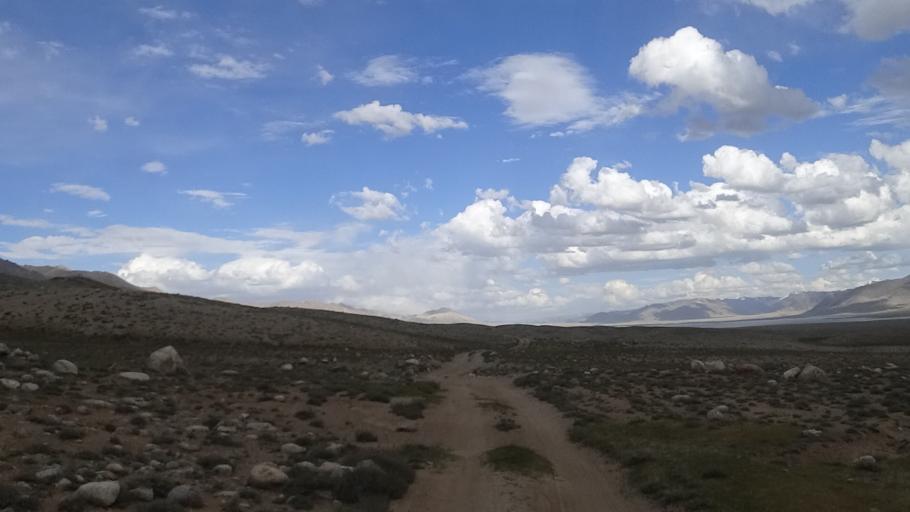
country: TJ
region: Gorno-Badakhshan
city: Murghob
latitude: 37.4690
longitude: 73.5960
